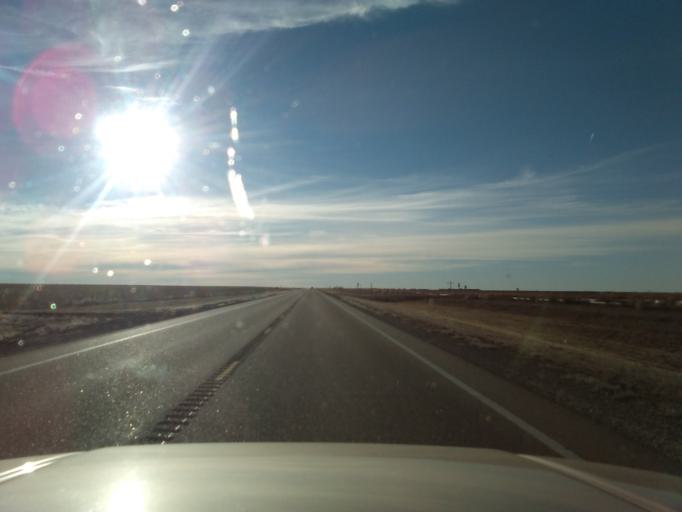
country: US
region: Kansas
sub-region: Sheridan County
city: Hoxie
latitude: 39.5247
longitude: -100.6129
